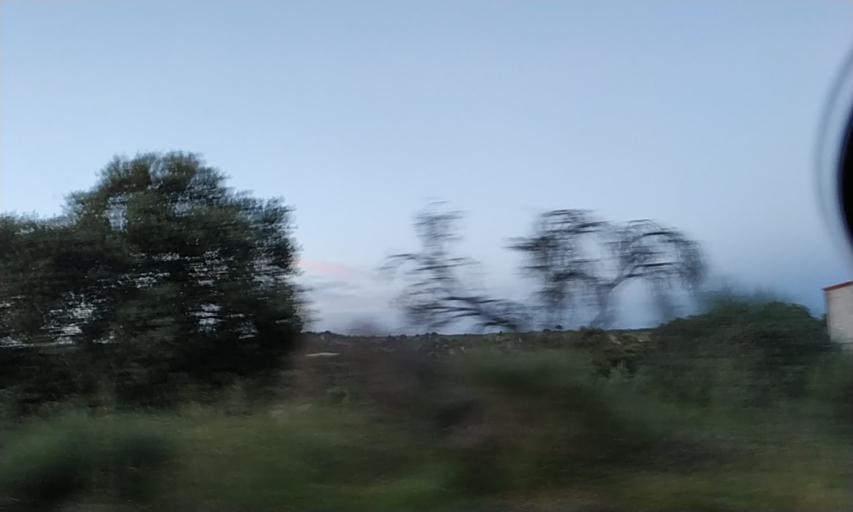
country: ES
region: Extremadura
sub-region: Provincia de Caceres
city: Piedras Albas
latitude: 39.7637
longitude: -6.9089
